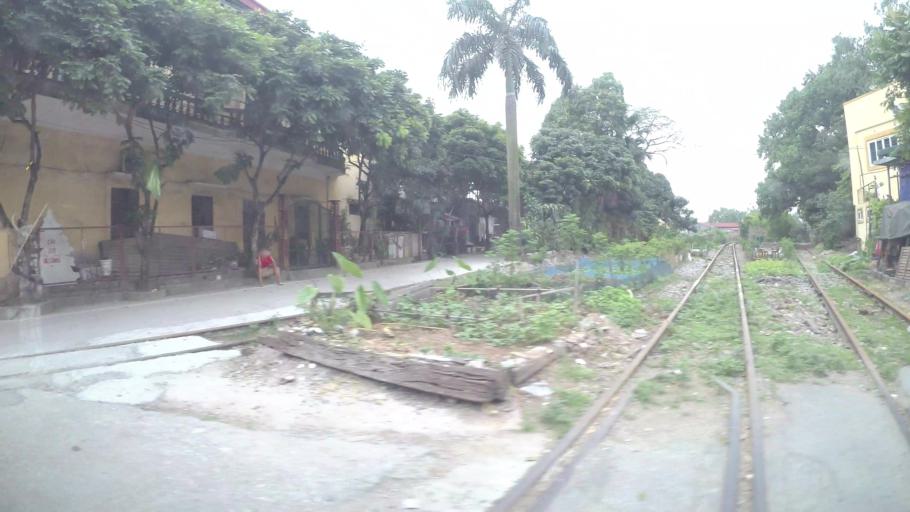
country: VN
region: Ha Noi
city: Hoan Kiem
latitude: 21.0643
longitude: 105.8927
